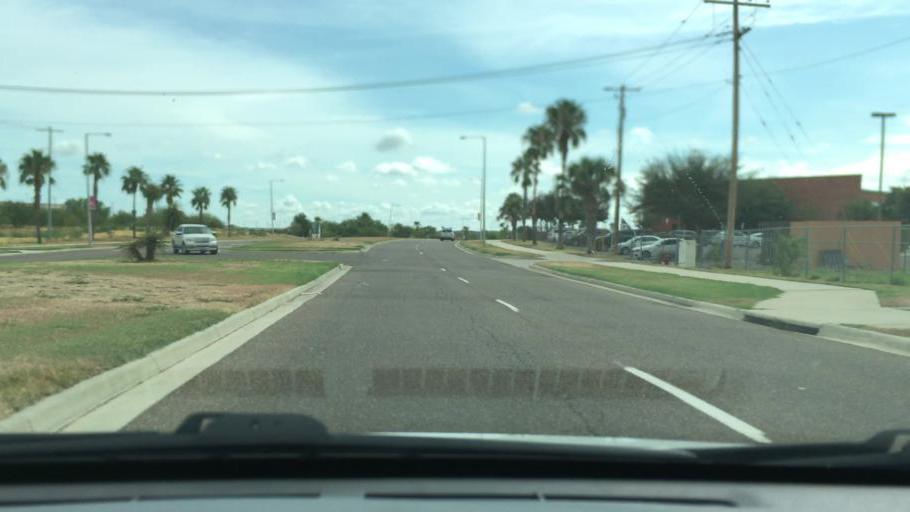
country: US
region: Texas
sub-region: Webb County
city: Laredo
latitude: 27.6038
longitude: -99.4810
